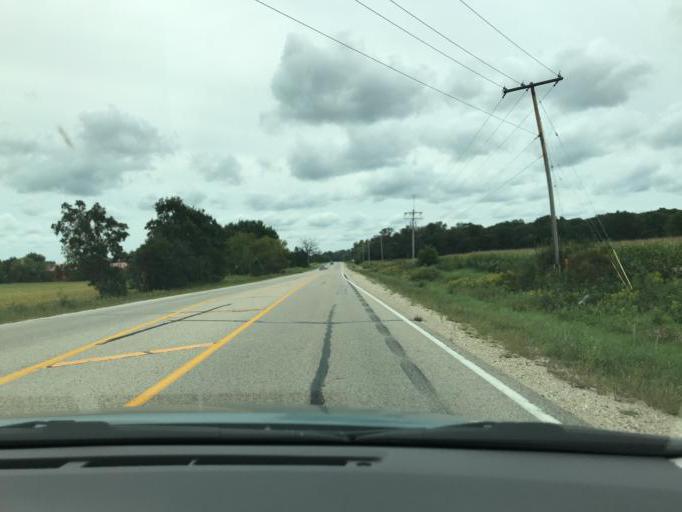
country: US
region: Wisconsin
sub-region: Racine County
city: Bohners Lake
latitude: 42.6401
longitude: -88.2501
